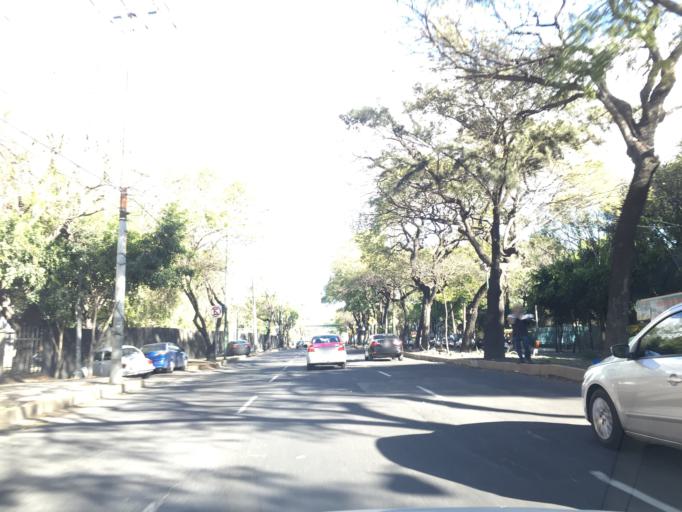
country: MX
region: Mexico
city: Colonia Lindavista
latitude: 19.4854
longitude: -99.1369
